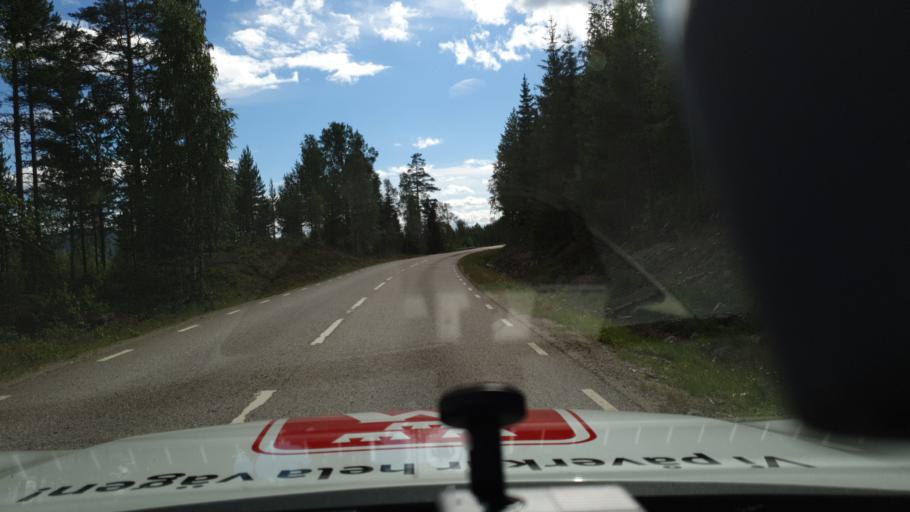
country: NO
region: Hedmark
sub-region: Trysil
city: Innbygda
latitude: 61.0332
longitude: 12.5845
